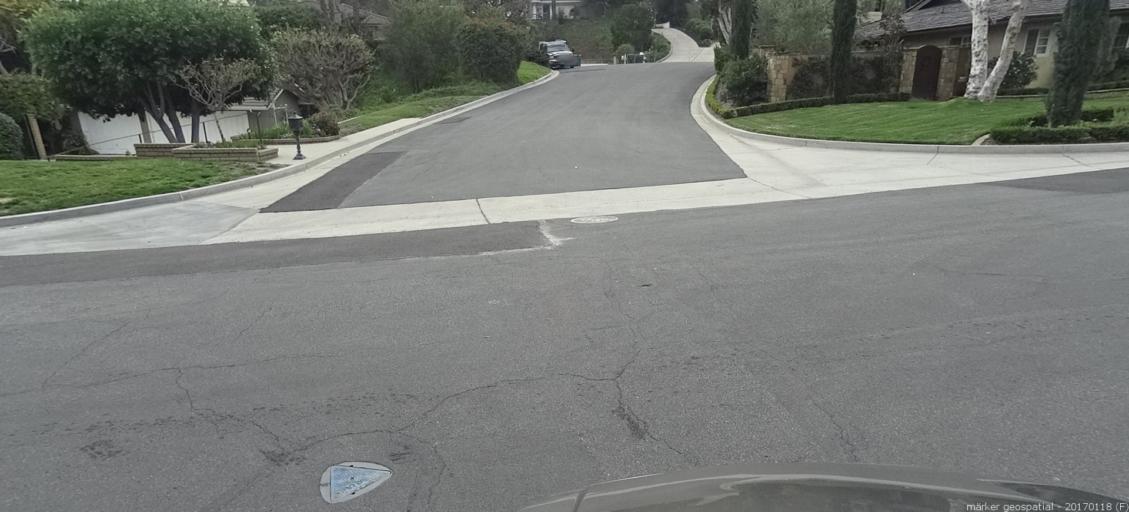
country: US
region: California
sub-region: Orange County
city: North Tustin
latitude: 33.7544
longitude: -117.7822
